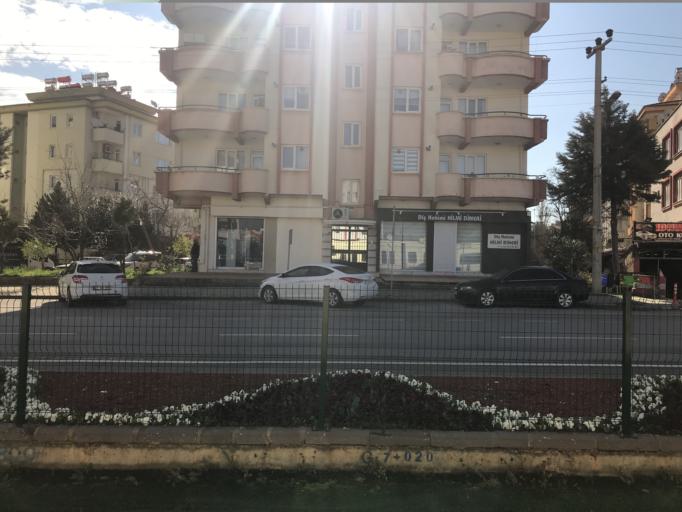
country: TR
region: Gaziantep
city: Sahinbey
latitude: 37.0445
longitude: 37.3239
